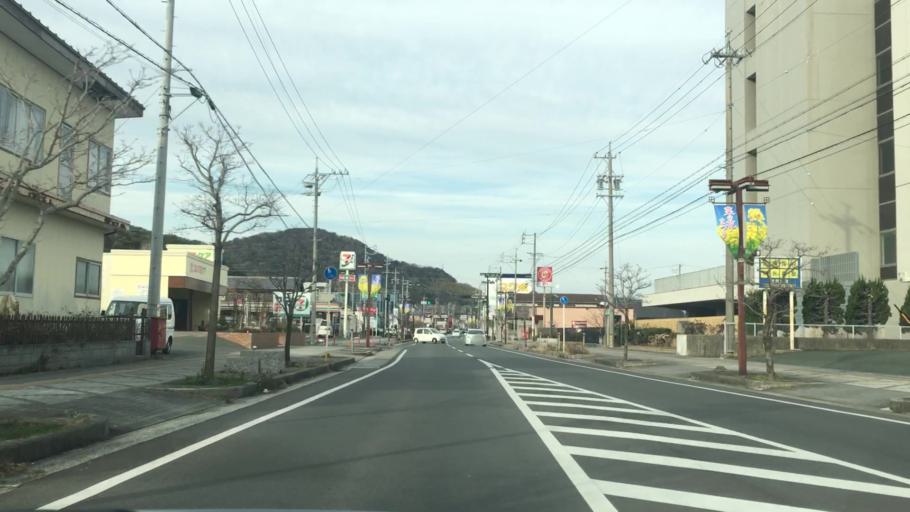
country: JP
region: Aichi
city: Tahara
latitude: 34.6715
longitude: 137.2702
